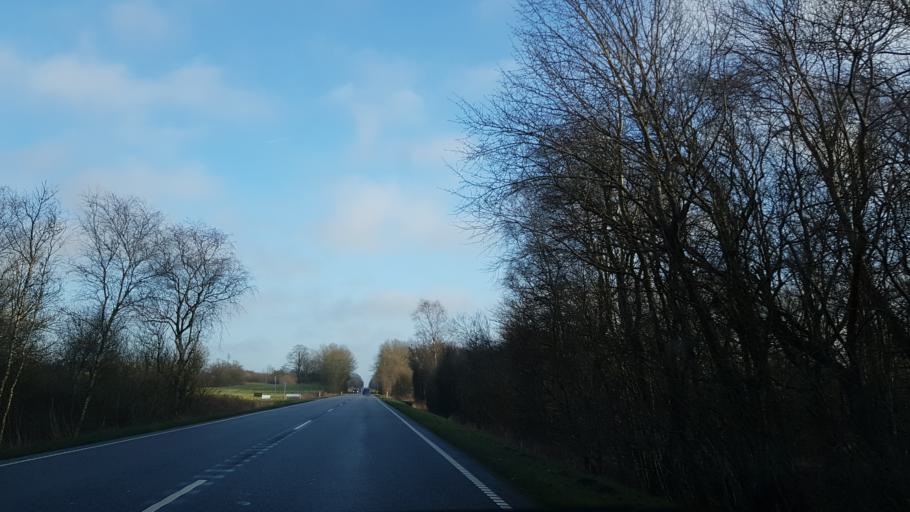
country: DK
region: South Denmark
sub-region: Haderslev Kommune
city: Vojens
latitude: 55.1722
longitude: 9.3499
